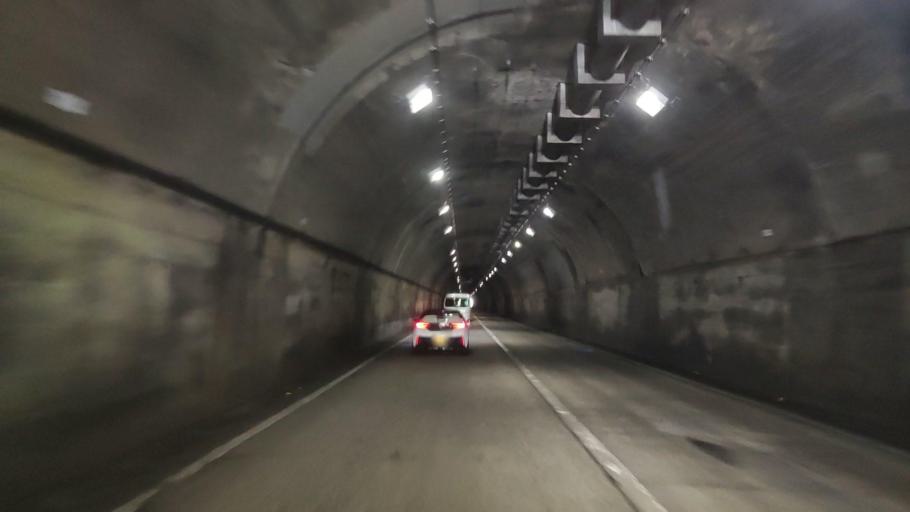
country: JP
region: Mie
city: Owase
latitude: 34.1567
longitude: 136.2660
